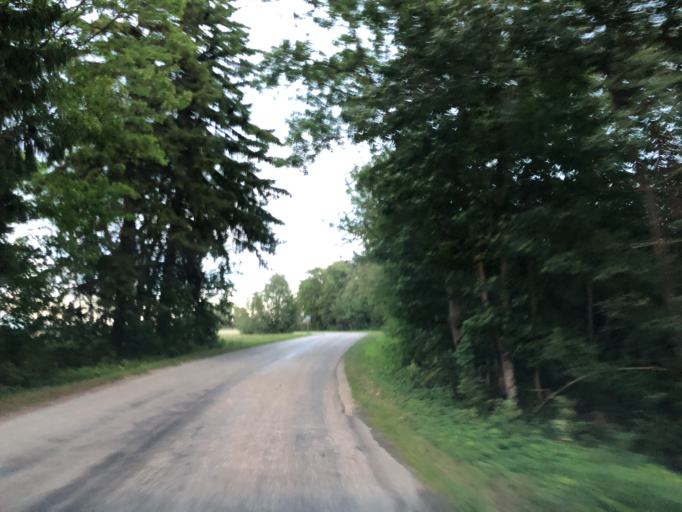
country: EE
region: Laeaene
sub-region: Ridala Parish
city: Uuemoisa
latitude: 58.8808
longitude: 23.6448
